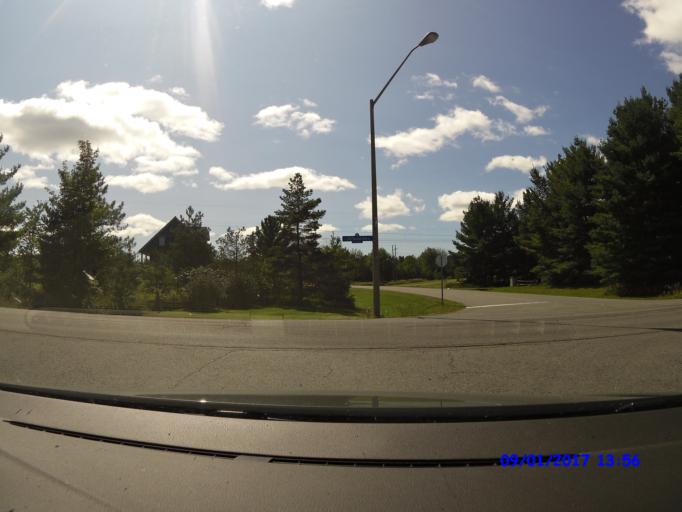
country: CA
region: Ontario
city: Bells Corners
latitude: 45.3576
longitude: -75.9607
